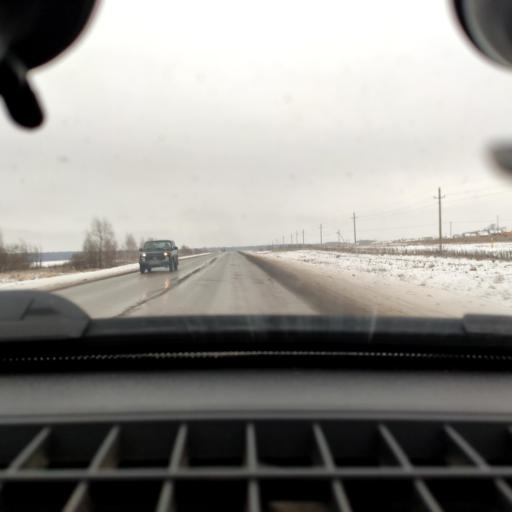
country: RU
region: Bashkortostan
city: Iglino
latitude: 54.8010
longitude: 56.4134
